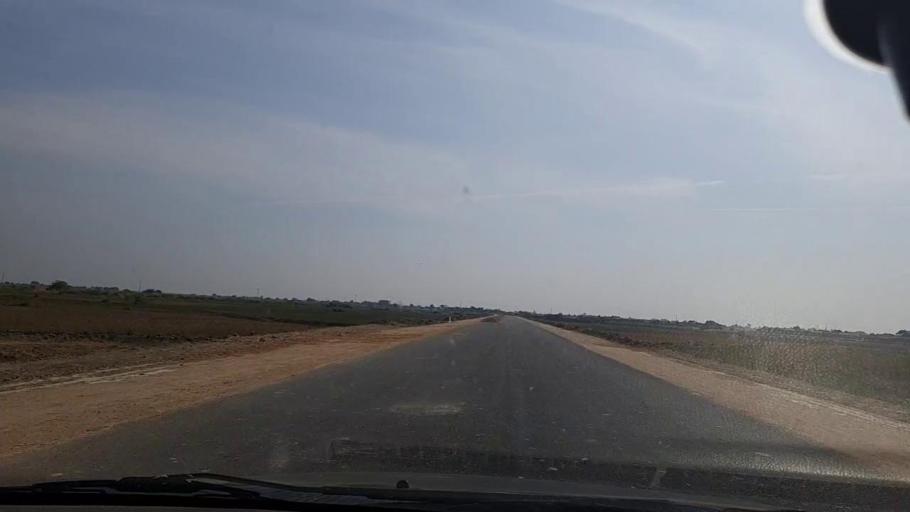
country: PK
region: Sindh
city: Mirpur Batoro
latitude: 24.7485
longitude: 68.2711
